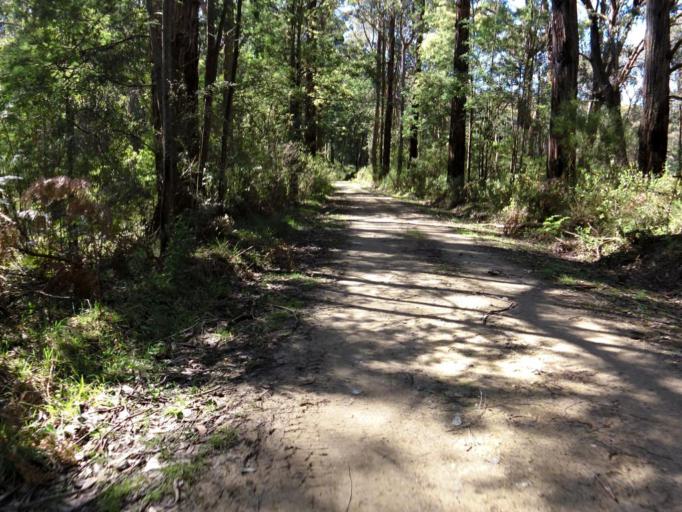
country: AU
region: Victoria
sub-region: Baw Baw
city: Warragul
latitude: -38.0554
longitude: 145.9591
